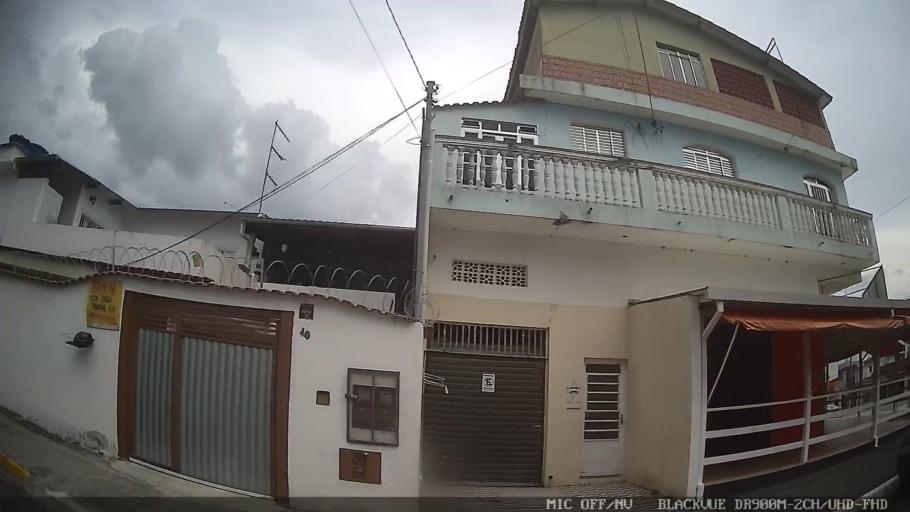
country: BR
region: Sao Paulo
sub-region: Suzano
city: Suzano
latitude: -23.5613
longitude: -46.2927
